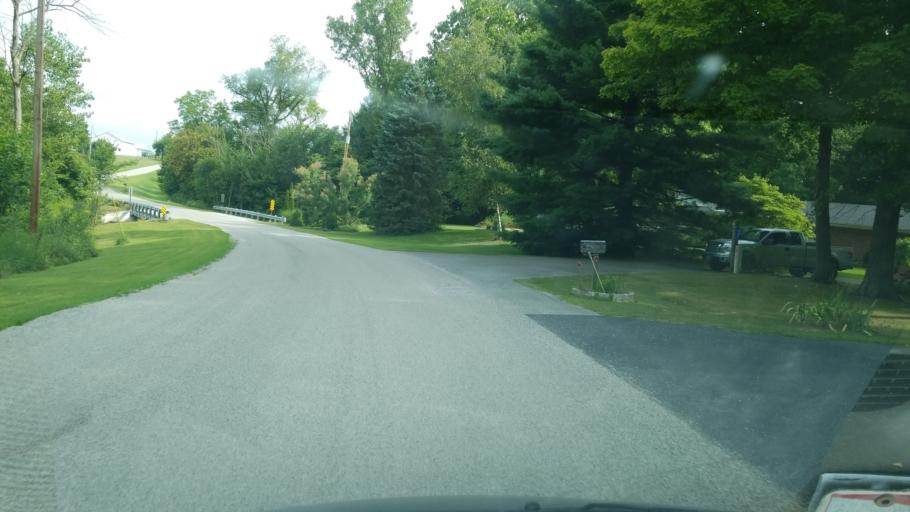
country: US
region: Ohio
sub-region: Seneca County
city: Tiffin
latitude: 41.1309
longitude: -83.0929
